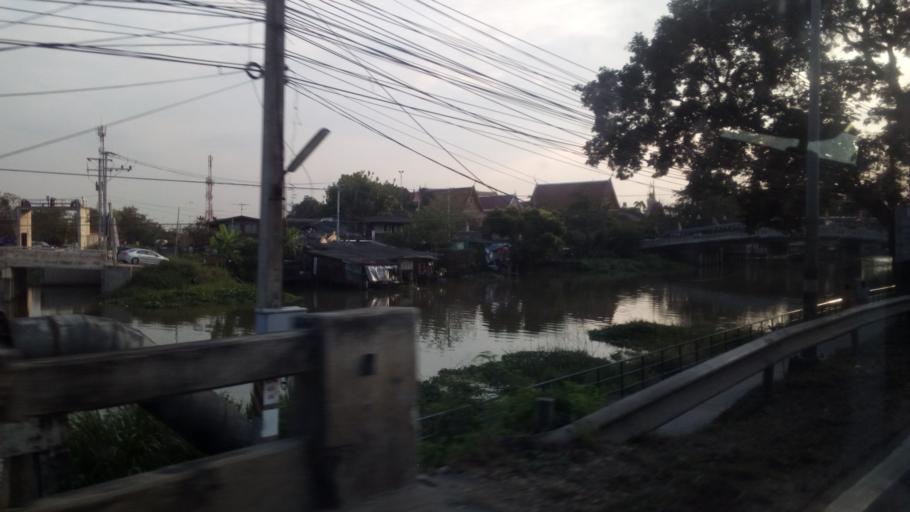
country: TH
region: Pathum Thani
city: Thanyaburi
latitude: 14.0092
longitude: 100.7093
